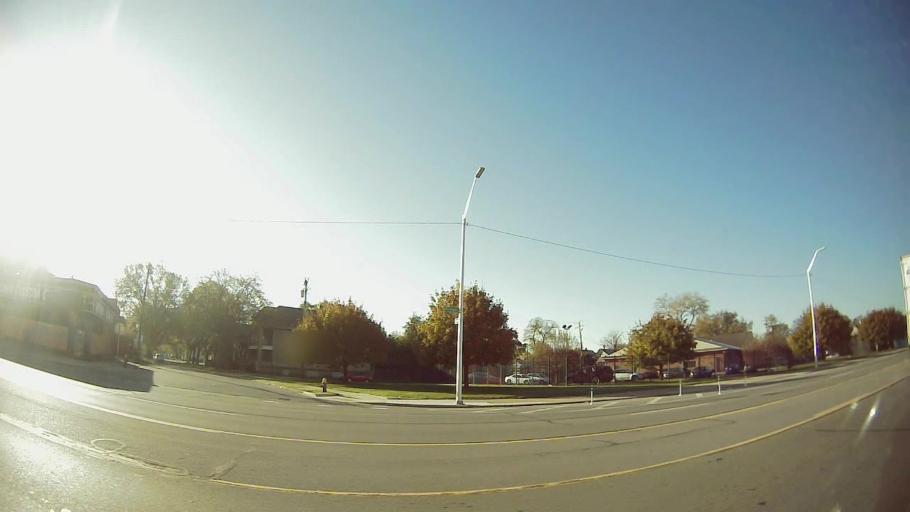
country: US
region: Michigan
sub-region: Wayne County
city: River Rouge
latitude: 42.3313
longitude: -83.1127
